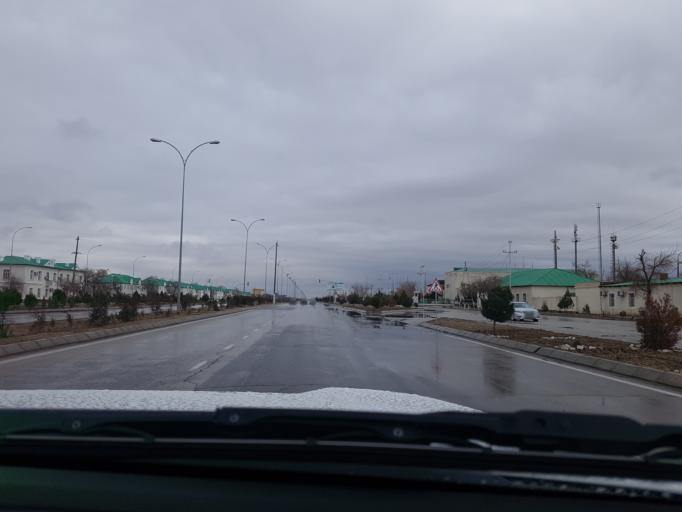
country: TM
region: Balkan
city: Balkanabat
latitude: 39.5061
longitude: 54.3538
